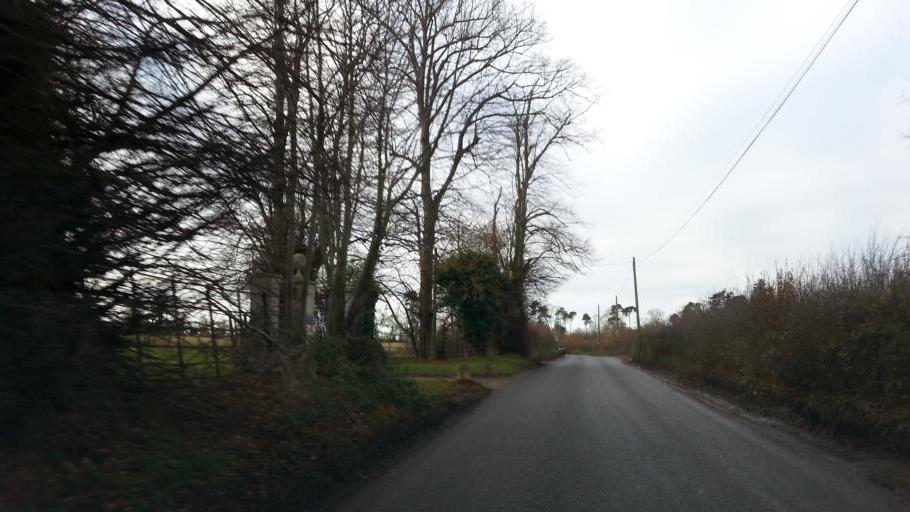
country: GB
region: England
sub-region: Suffolk
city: Wickham Market
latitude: 52.1525
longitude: 1.4161
